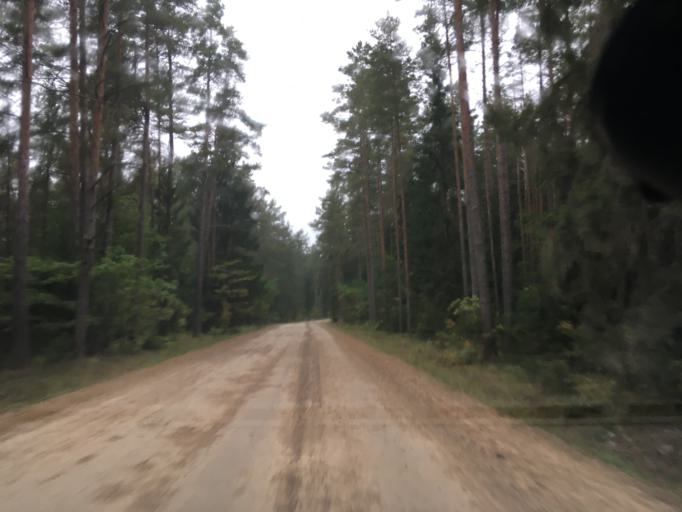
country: LV
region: Kuldigas Rajons
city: Kuldiga
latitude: 56.9897
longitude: 21.9743
